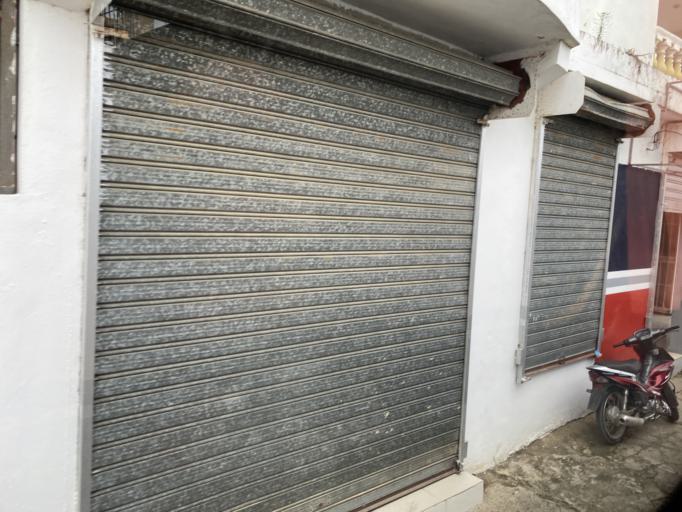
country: DO
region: El Seibo
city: Miches
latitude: 18.9842
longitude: -69.0493
